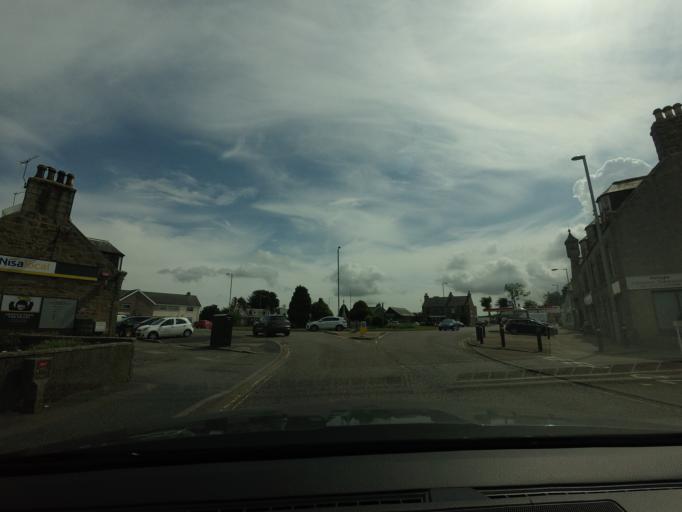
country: GB
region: Scotland
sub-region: Aberdeenshire
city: Mintlaw
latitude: 57.5251
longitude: -2.0023
